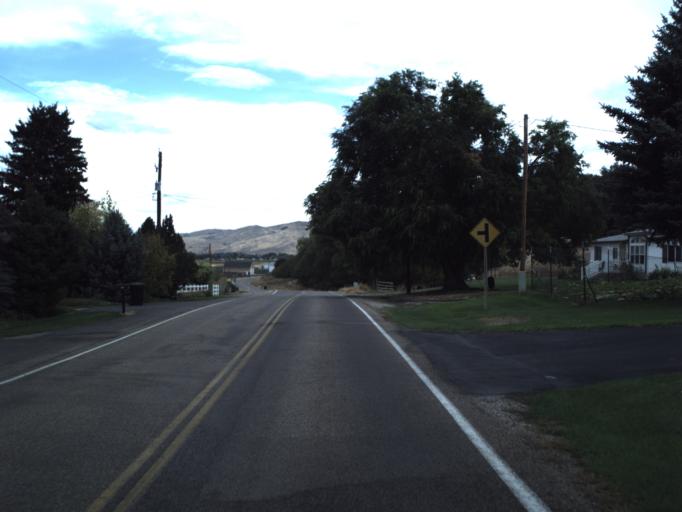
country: US
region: Utah
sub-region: Morgan County
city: Morgan
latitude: 41.0068
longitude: -111.6758
